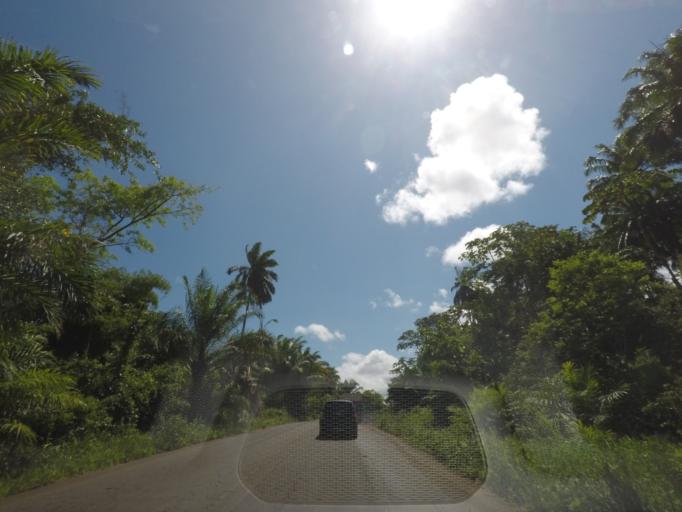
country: BR
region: Bahia
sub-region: Valenca
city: Valenca
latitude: -13.4453
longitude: -39.0828
